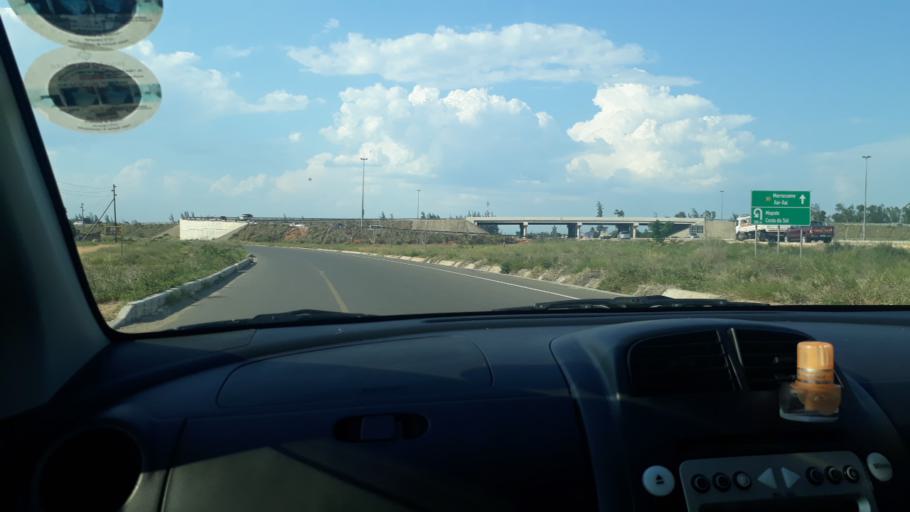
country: MZ
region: Maputo City
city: Maputo
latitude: -25.8202
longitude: 32.5711
